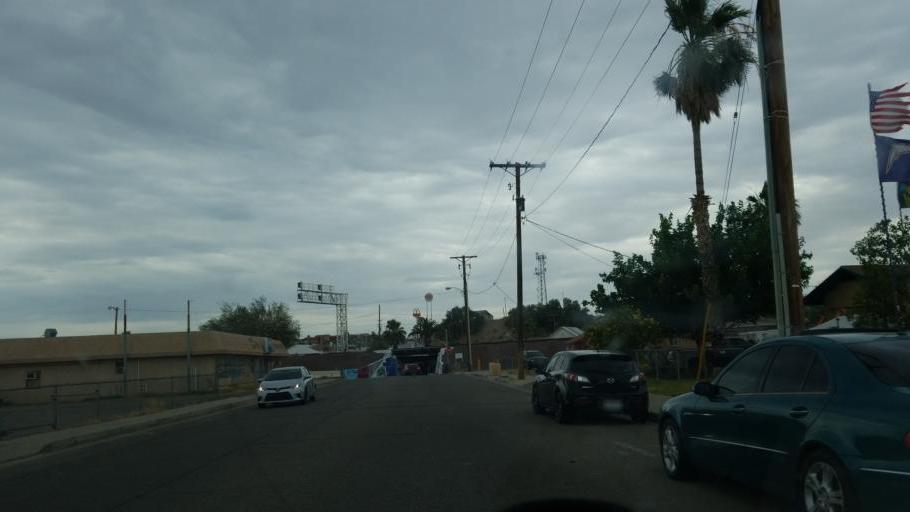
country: US
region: California
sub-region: San Bernardino County
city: Needles
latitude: 34.8441
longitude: -114.6105
